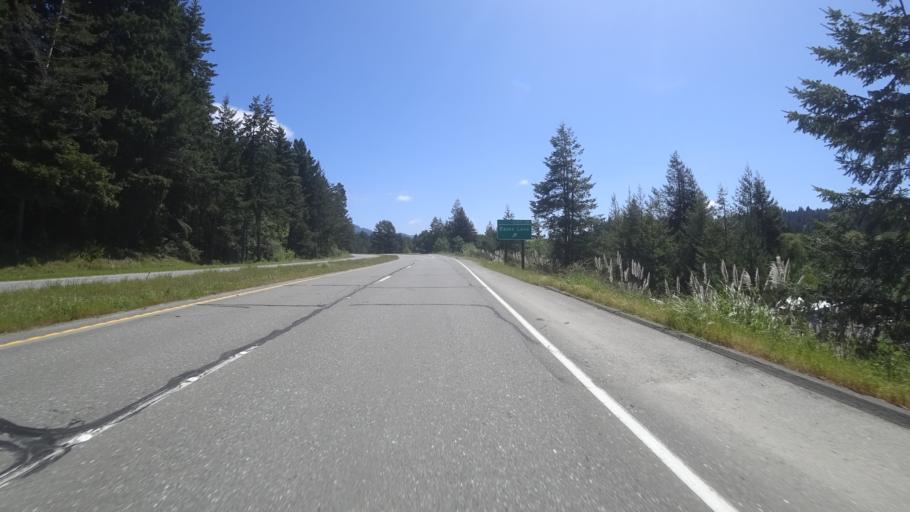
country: US
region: California
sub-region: Humboldt County
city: Arcata
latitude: 40.9073
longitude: -124.0432
